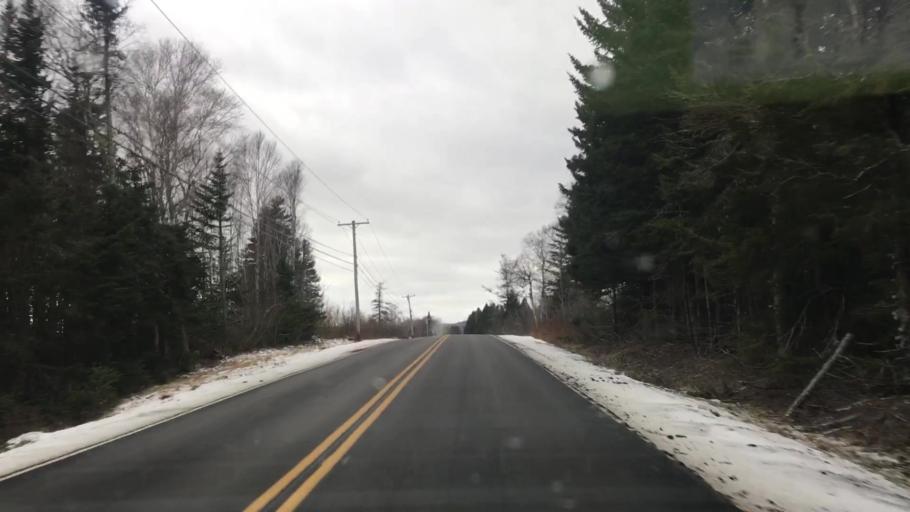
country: US
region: Maine
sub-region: Washington County
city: Machiasport
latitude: 44.7031
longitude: -67.3353
